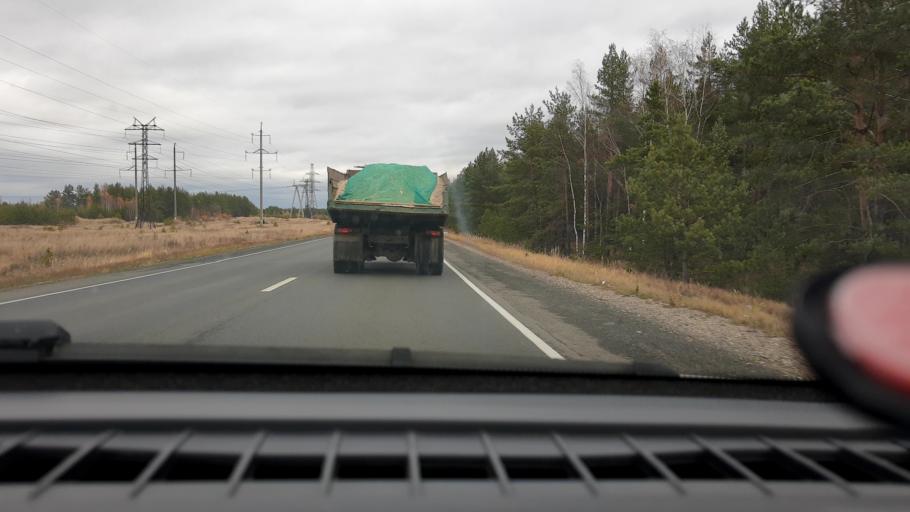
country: RU
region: Nizjnij Novgorod
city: Lukino
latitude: 56.3822
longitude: 43.6325
